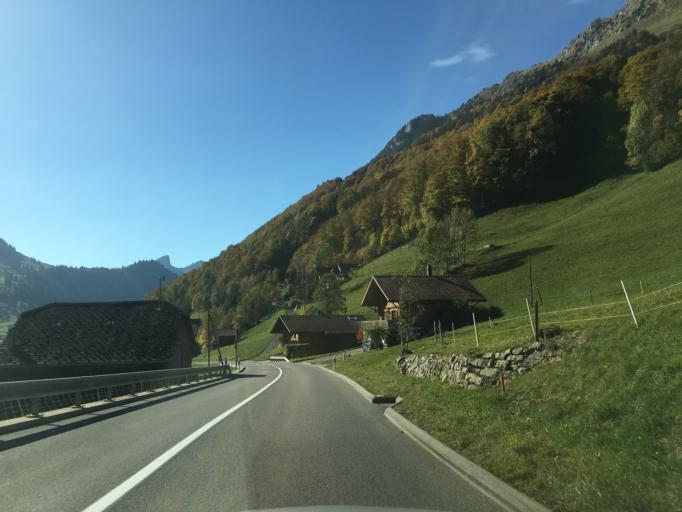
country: CH
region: Fribourg
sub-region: Gruyere District
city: Charmey
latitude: 46.6047
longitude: 7.2546
